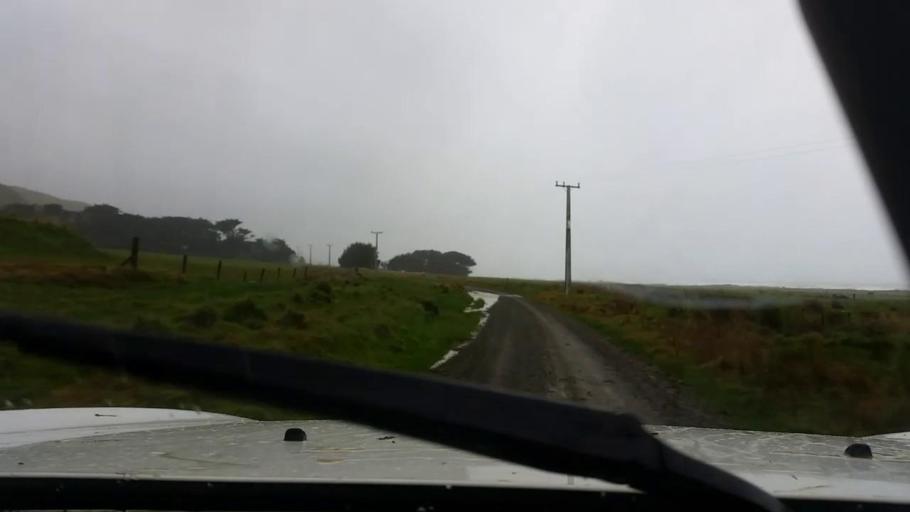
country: NZ
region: Wellington
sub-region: Masterton District
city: Masterton
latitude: -41.2595
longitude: 175.8985
